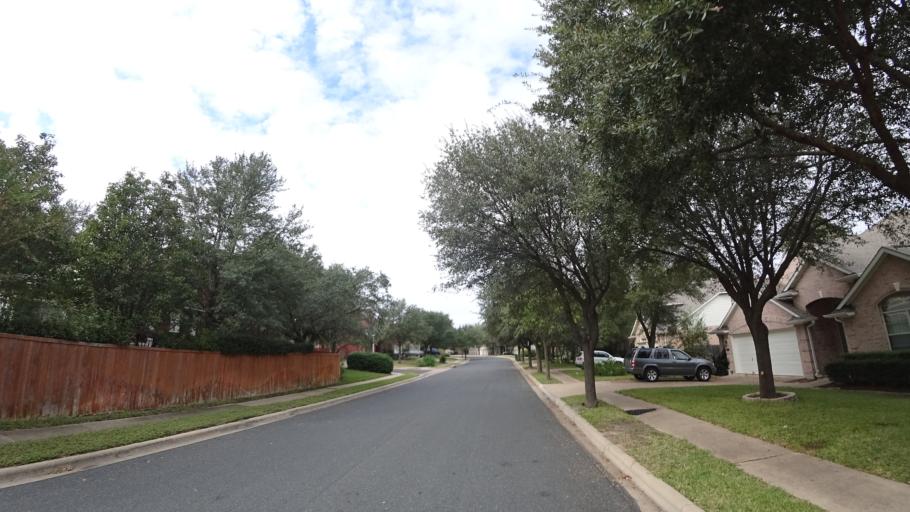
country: US
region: Texas
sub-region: Travis County
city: Wells Branch
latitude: 30.4264
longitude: -97.6861
